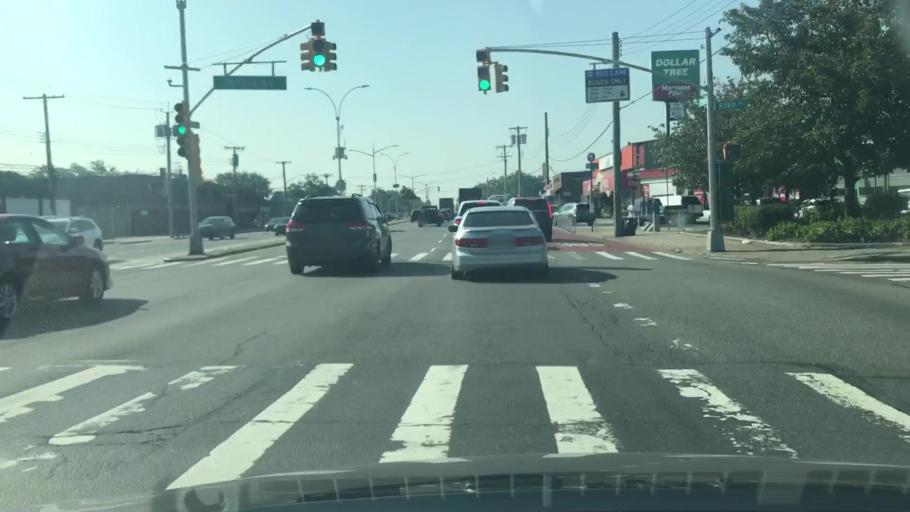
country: US
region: New York
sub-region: Queens County
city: Borough of Queens
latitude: 40.6723
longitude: -73.8434
